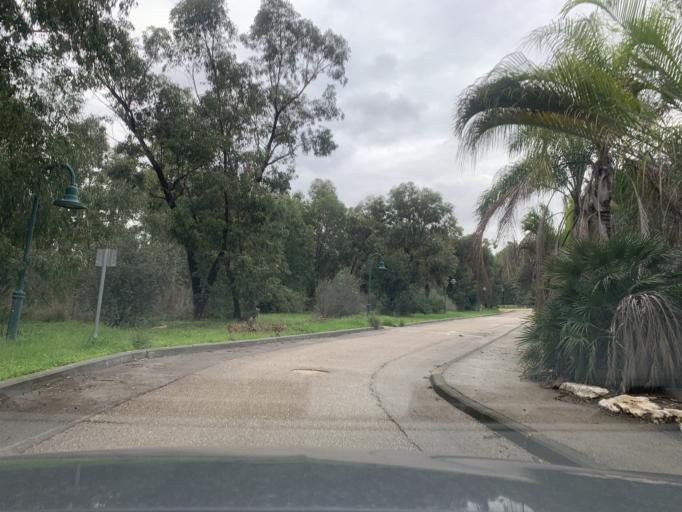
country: PS
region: West Bank
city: Qalqilyah
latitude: 32.2140
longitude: 34.9814
